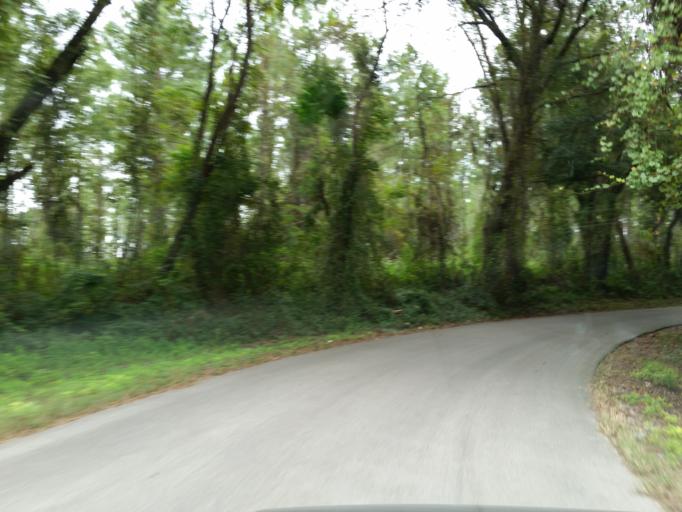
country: US
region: Florida
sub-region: Alachua County
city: High Springs
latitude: 29.9858
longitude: -82.5636
